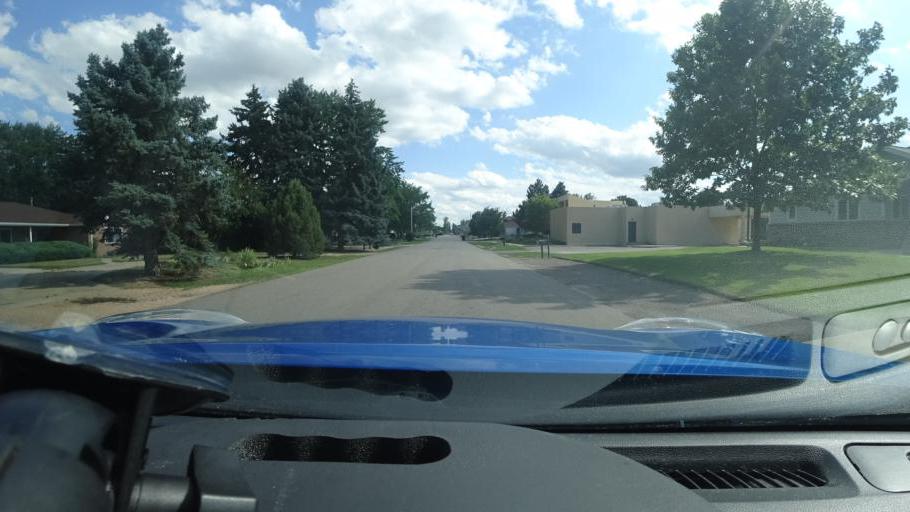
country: US
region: Colorado
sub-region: Adams County
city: Aurora
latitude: 39.6983
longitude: -104.8707
